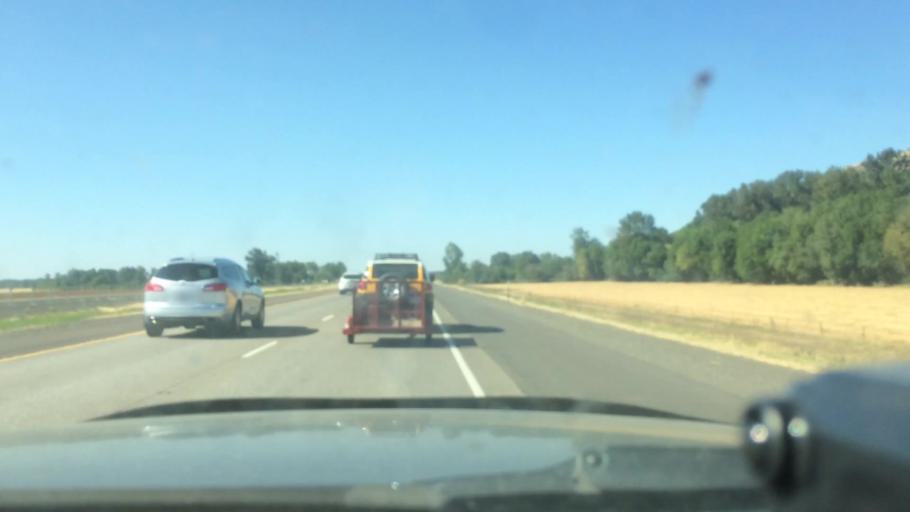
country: US
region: Oregon
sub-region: Linn County
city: Brownsville
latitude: 44.4493
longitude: -123.0604
